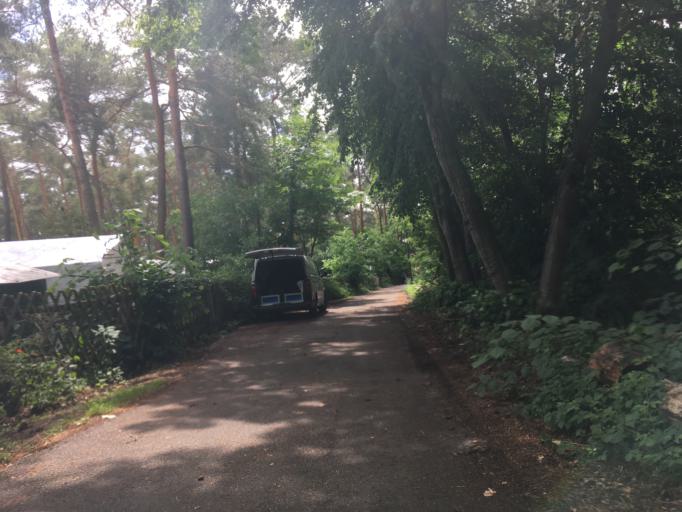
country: DE
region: Berlin
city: Schmockwitz
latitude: 52.3912
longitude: 13.6520
